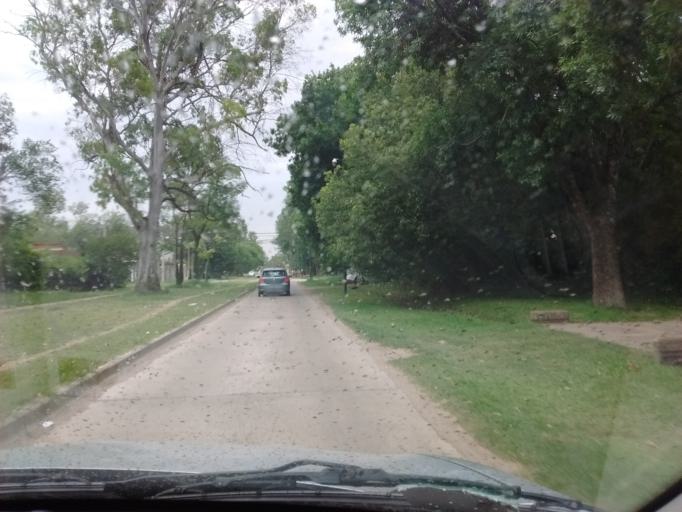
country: AR
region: Santa Fe
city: Funes
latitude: -32.9217
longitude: -60.8004
